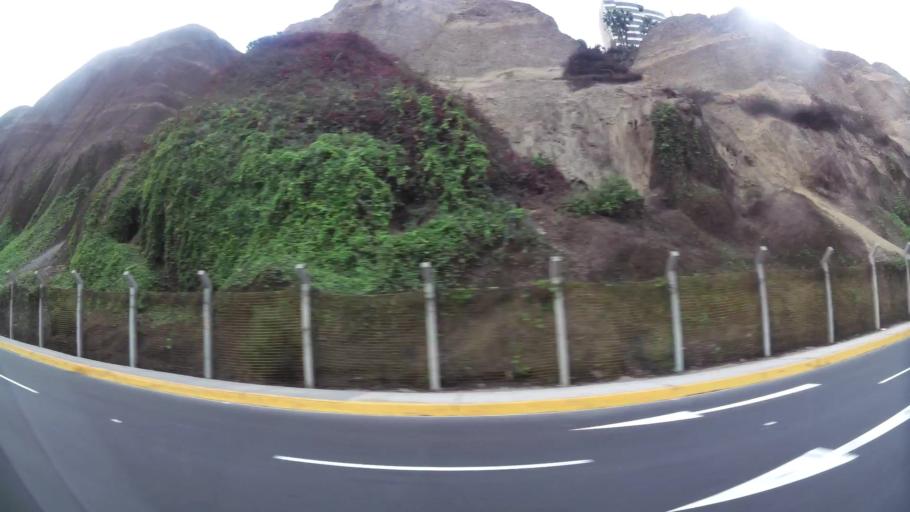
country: PE
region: Lima
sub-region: Lima
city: Surco
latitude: -12.1365
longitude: -77.0286
